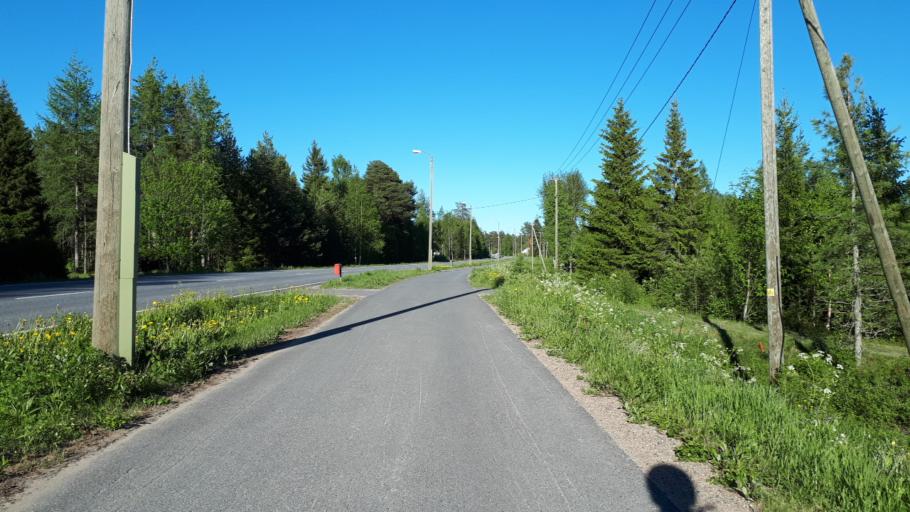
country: FI
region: Northern Ostrobothnia
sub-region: Oulunkaari
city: Ii
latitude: 65.3250
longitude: 25.4989
